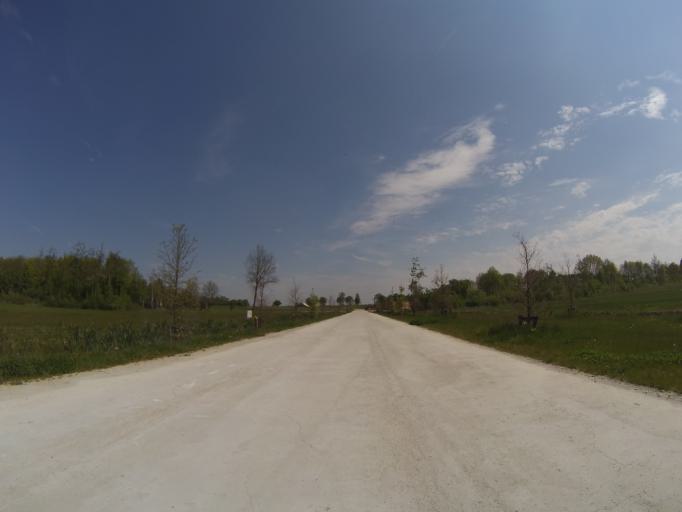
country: NL
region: Flevoland
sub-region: Gemeente Zeewolde
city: Zeewolde
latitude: 52.2845
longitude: 5.5266
